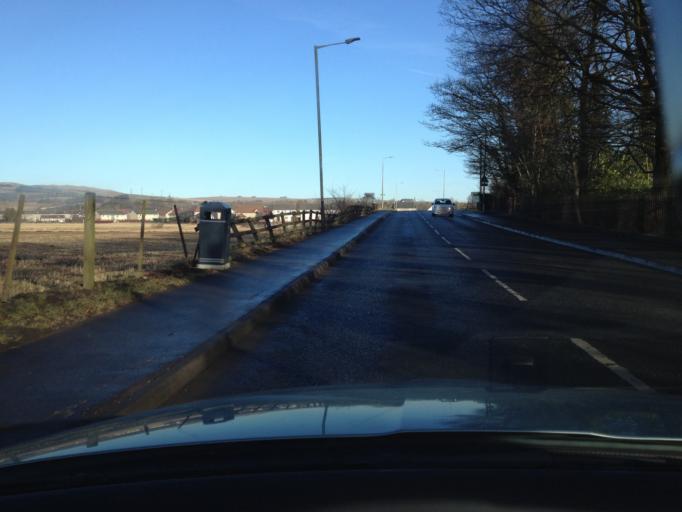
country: GB
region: Scotland
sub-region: Perth and Kinross
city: Milnathort
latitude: 56.2202
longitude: -3.4252
